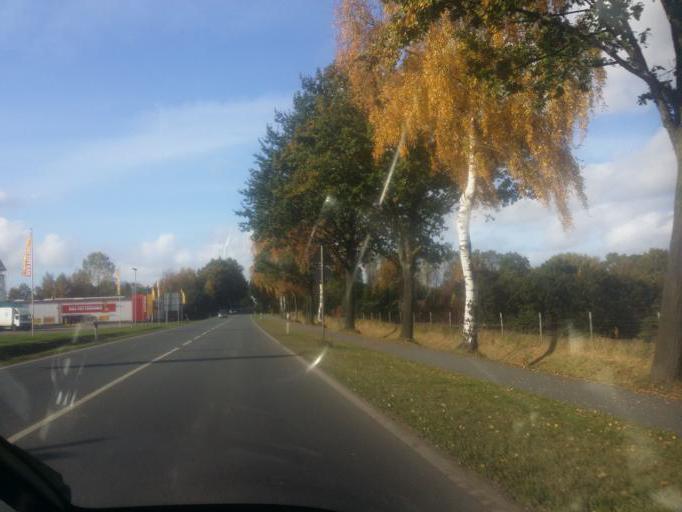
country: DE
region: Schleswig-Holstein
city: Elmshorn
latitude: 53.7764
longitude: 9.6599
